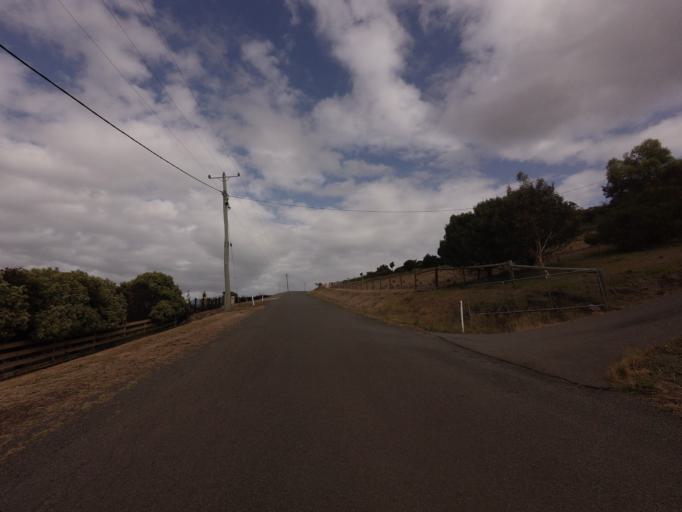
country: AU
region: Tasmania
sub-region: Clarence
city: Acton Park
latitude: -42.8580
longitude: 147.4658
